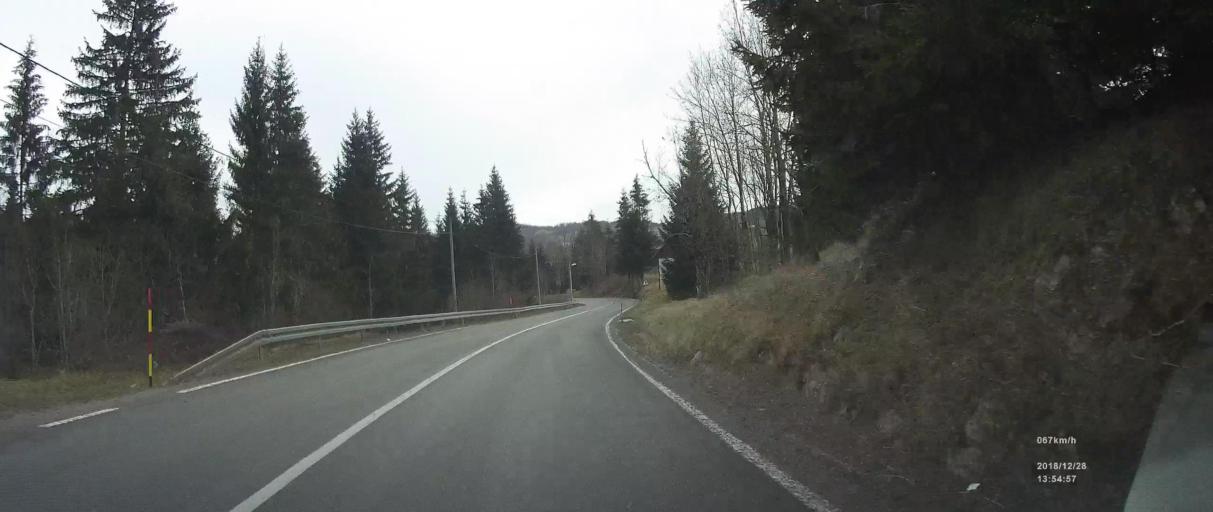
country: HR
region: Primorsko-Goranska
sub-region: Grad Delnice
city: Delnice
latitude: 45.3831
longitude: 14.8695
